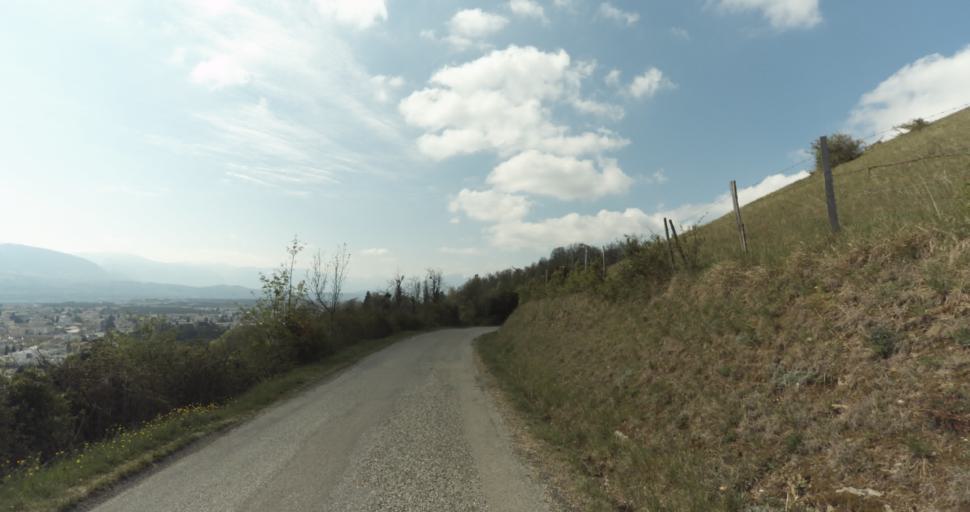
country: FR
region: Rhone-Alpes
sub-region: Departement de l'Isere
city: Saint-Marcellin
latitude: 45.1630
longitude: 5.3133
